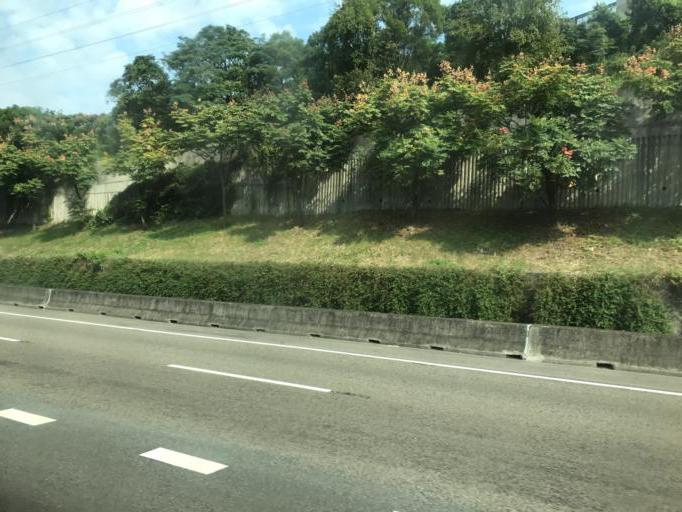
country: TW
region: Taiwan
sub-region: Hsinchu
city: Hsinchu
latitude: 24.7793
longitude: 121.0036
